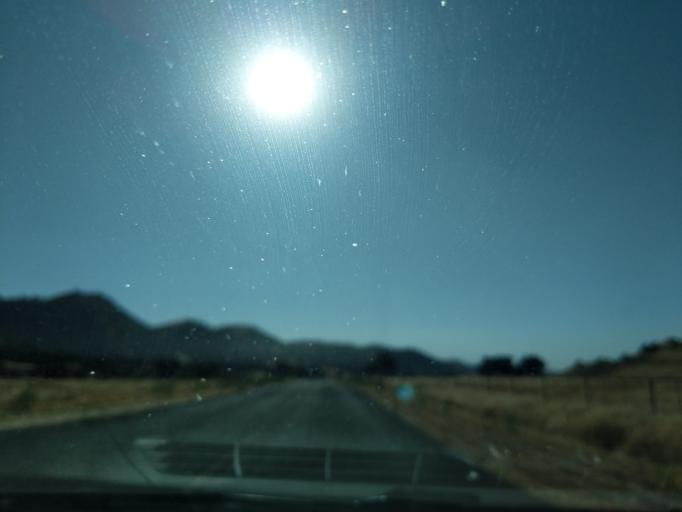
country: US
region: California
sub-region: Monterey County
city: King City
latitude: 36.1871
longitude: -120.8162
